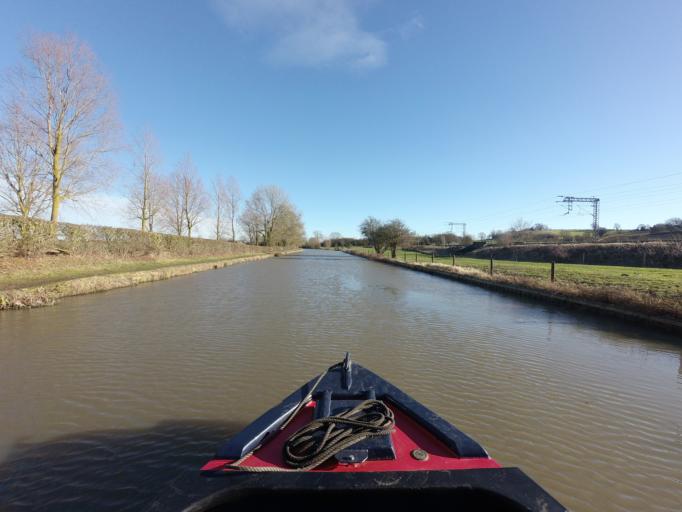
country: GB
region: England
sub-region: Northamptonshire
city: Bugbrooke
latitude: 52.2018
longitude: -1.0086
